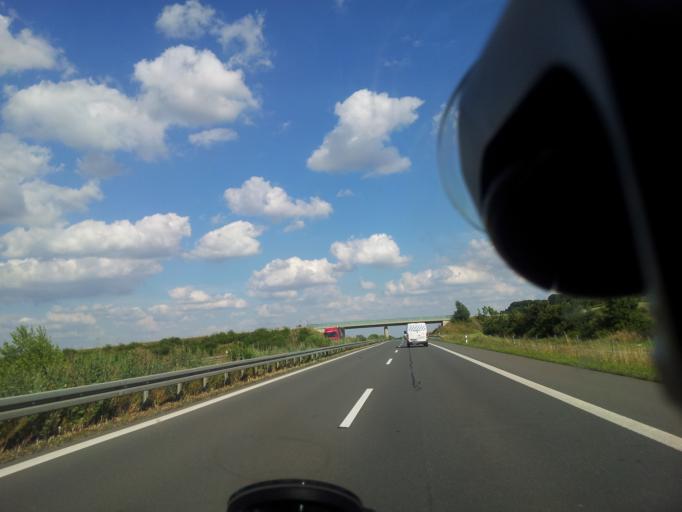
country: DE
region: Saxony-Anhalt
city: Heudeber
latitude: 51.8452
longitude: 10.8391
